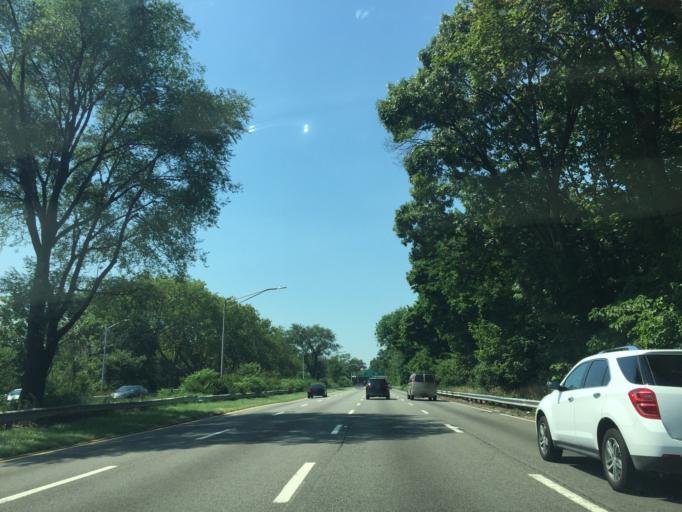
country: US
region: New York
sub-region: Nassau County
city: South Valley Stream
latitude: 40.6717
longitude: -73.7362
